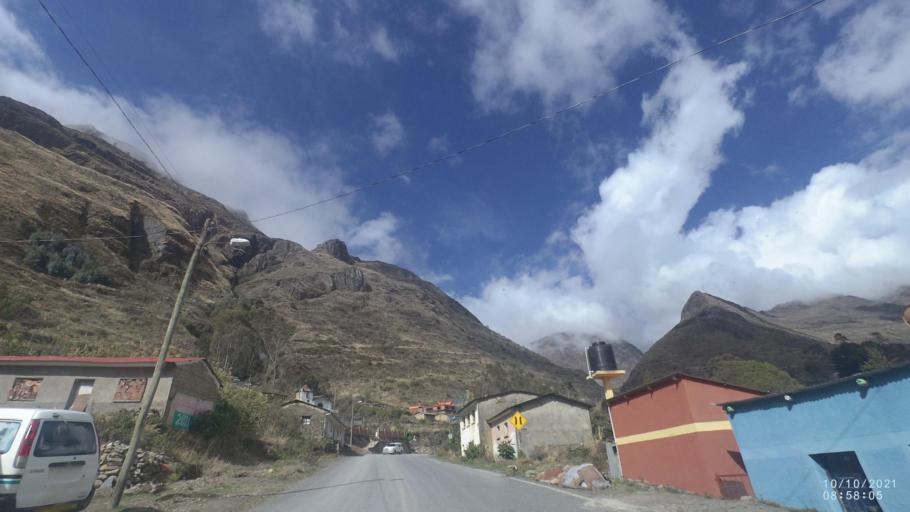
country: BO
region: La Paz
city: Quime
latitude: -16.9976
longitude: -67.2547
